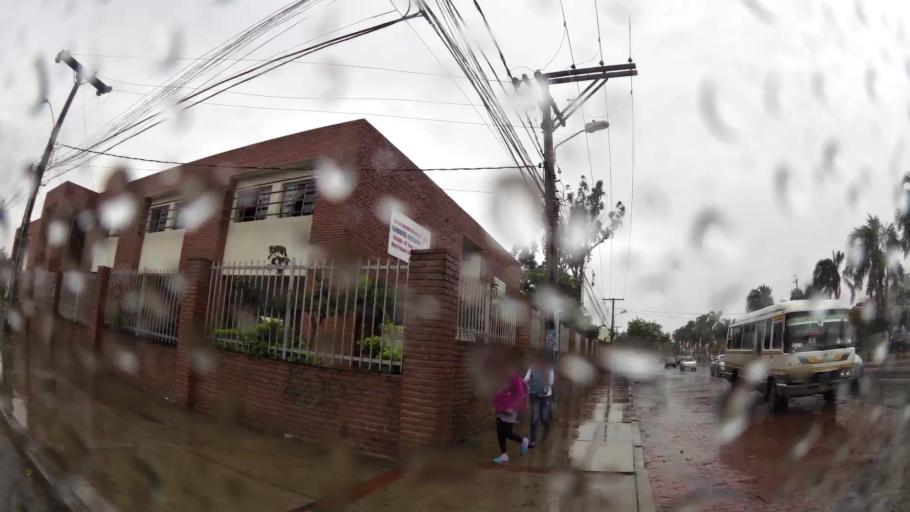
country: BO
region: Santa Cruz
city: Santa Cruz de la Sierra
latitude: -17.7851
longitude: -63.2012
